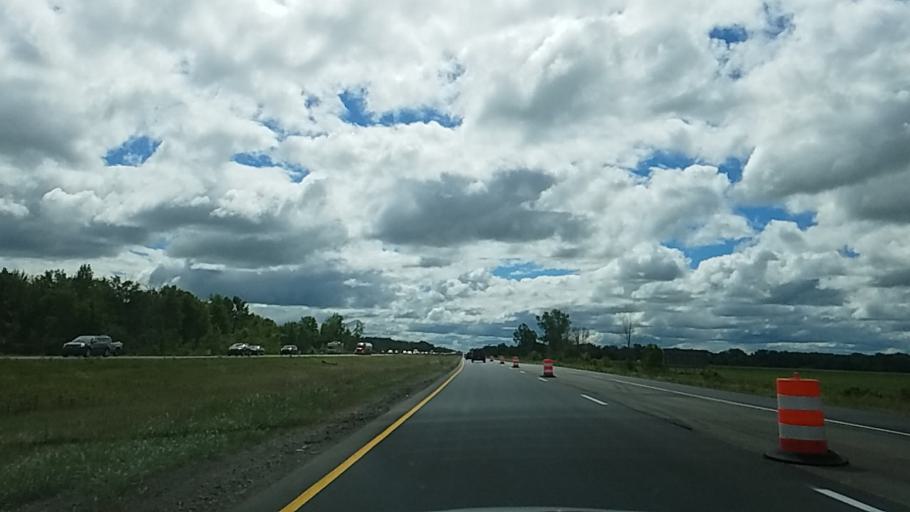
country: US
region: Michigan
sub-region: Bay County
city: Pinconning
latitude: 43.9196
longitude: -84.0206
